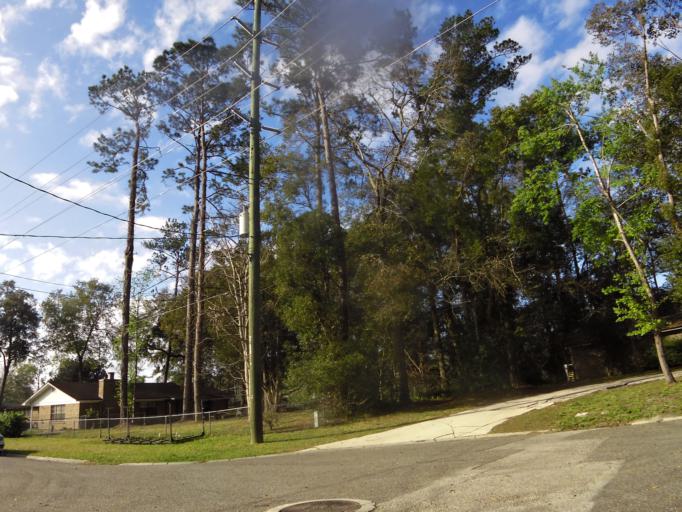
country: US
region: Florida
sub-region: Duval County
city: Jacksonville
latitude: 30.2850
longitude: -81.6125
